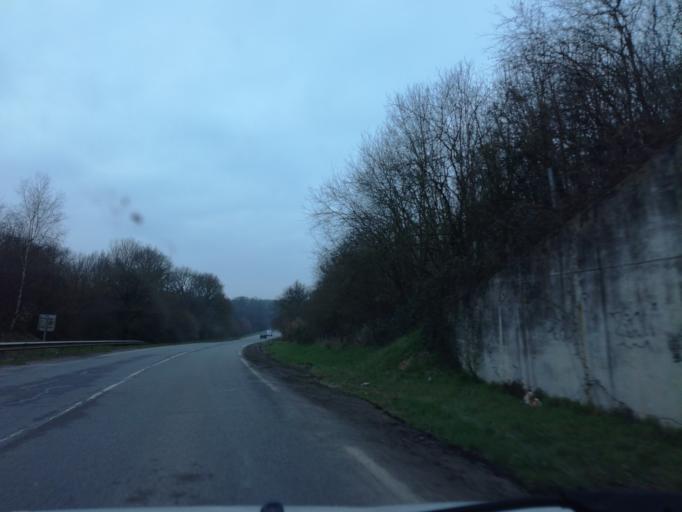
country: FR
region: Brittany
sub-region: Departement d'Ille-et-Vilaine
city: Gosne
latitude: 48.2402
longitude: -1.4615
